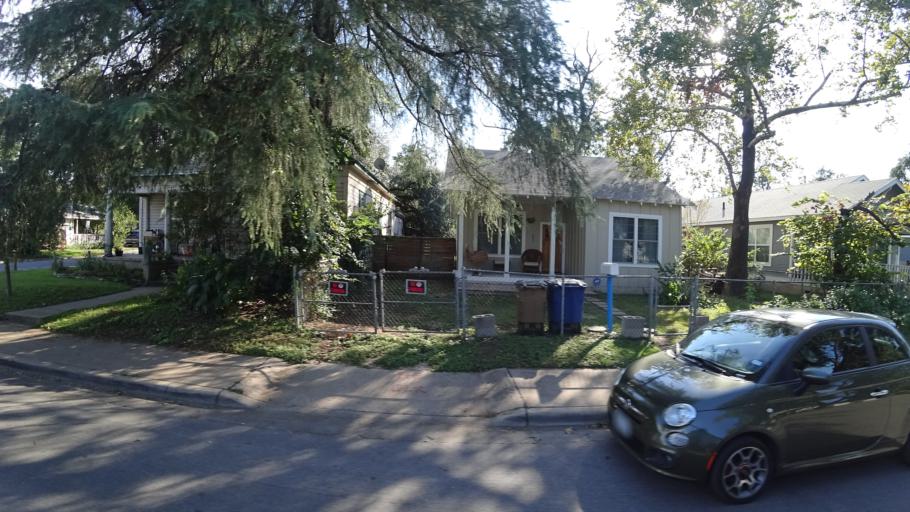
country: US
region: Texas
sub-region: Travis County
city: Austin
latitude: 30.2574
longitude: -97.7226
